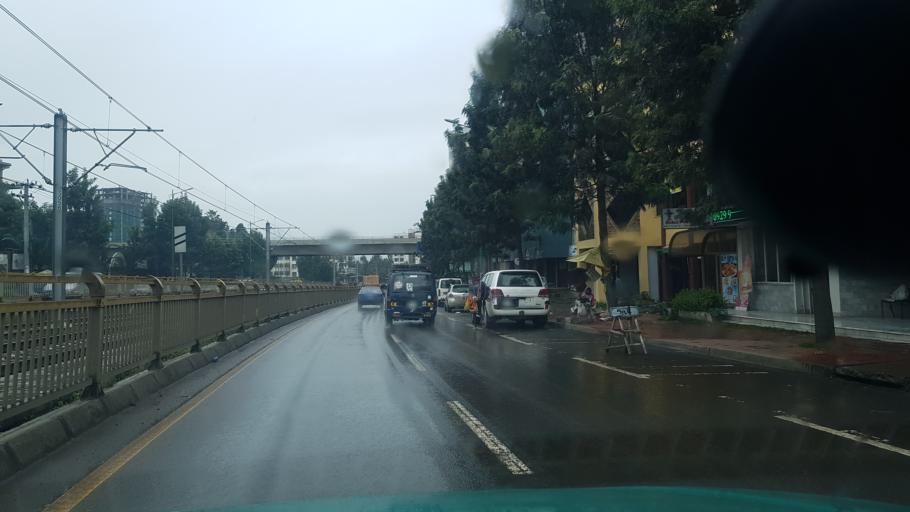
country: ET
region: Adis Abeba
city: Addis Ababa
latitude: 8.9973
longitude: 38.7593
